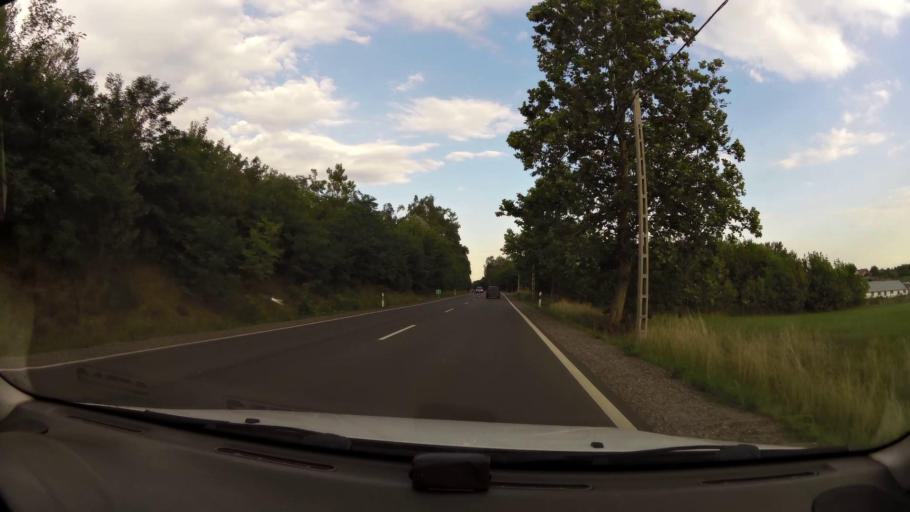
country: HU
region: Pest
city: Gyomro
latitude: 47.4397
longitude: 19.4037
